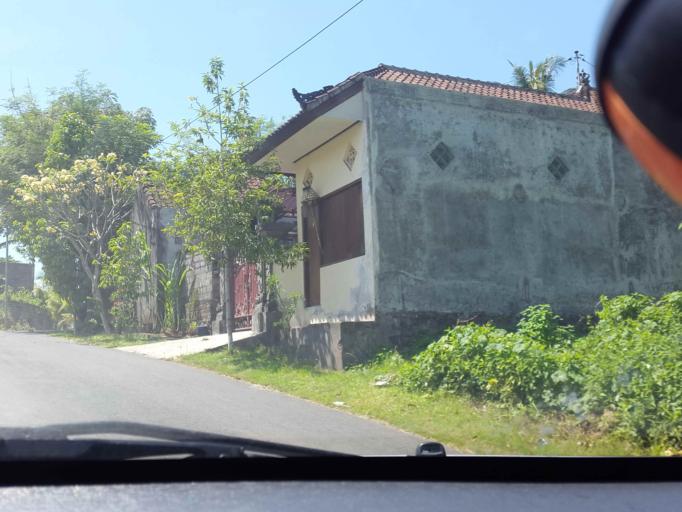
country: ID
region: Bali
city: Klungkung
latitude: -8.5373
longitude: 115.3934
